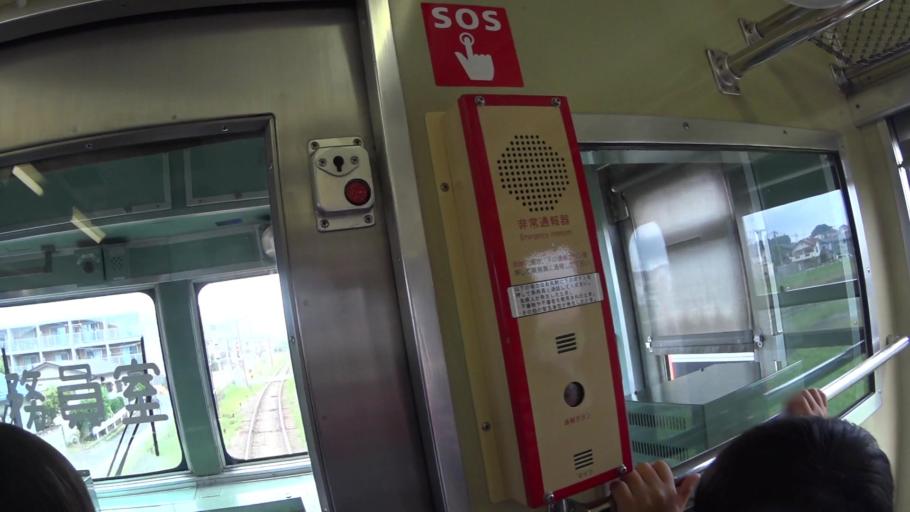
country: JP
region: Chiba
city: Nagareyama
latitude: 35.8401
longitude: 139.9090
